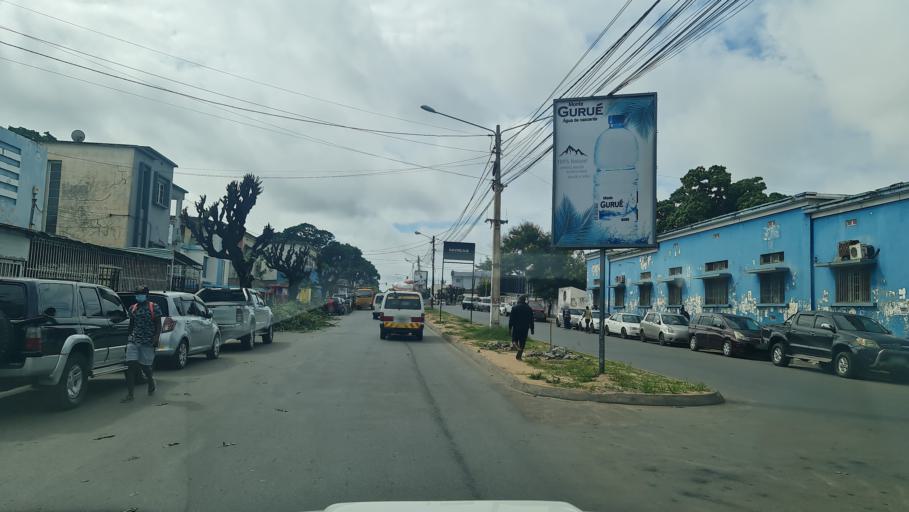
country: MZ
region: Nampula
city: Nampula
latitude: -15.1136
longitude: 39.2602
